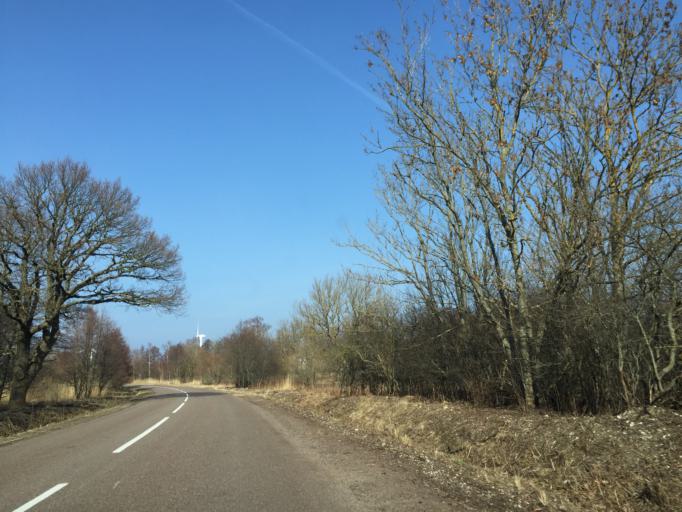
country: EE
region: Saare
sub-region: Kuressaare linn
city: Kuressaare
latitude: 57.9815
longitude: 22.0208
